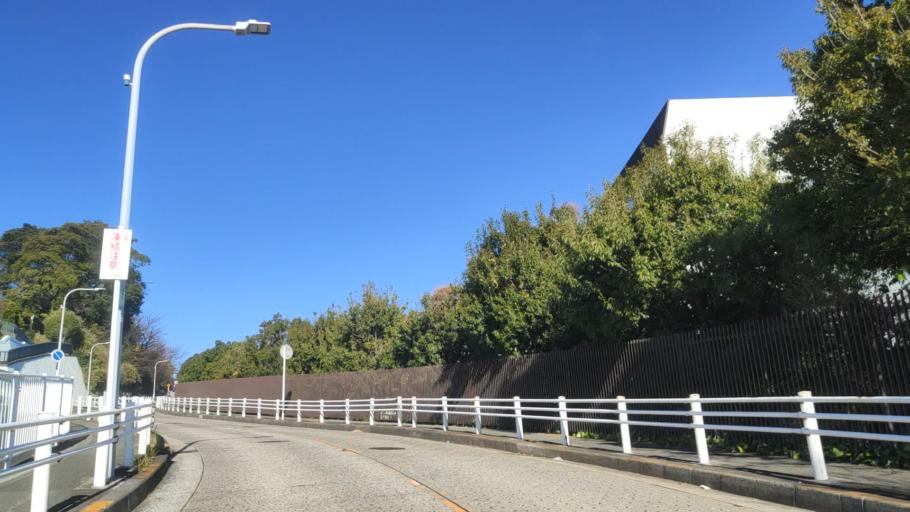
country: JP
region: Kanagawa
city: Yokohama
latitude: 35.4217
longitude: 139.6564
